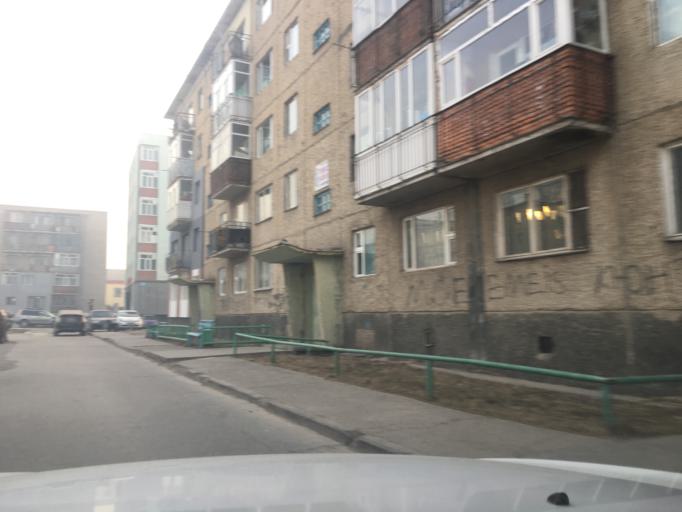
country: MN
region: Ulaanbaatar
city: Ulaanbaatar
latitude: 47.9163
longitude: 106.8134
